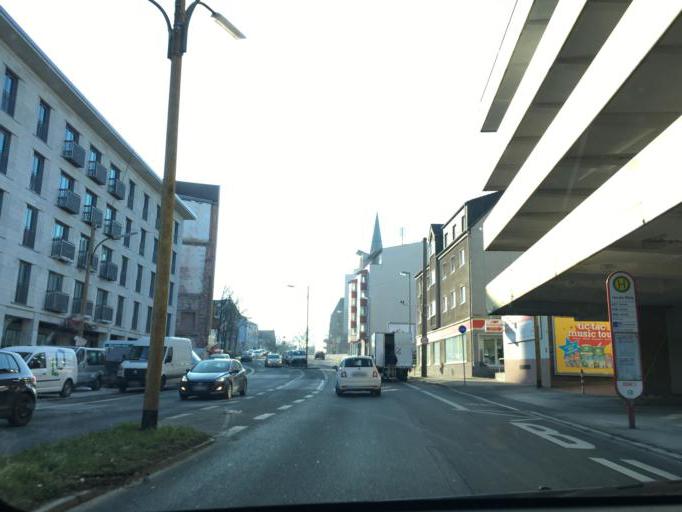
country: DE
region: North Rhine-Westphalia
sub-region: Regierungsbezirk Arnsberg
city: Dortmund
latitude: 51.4908
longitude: 7.5029
